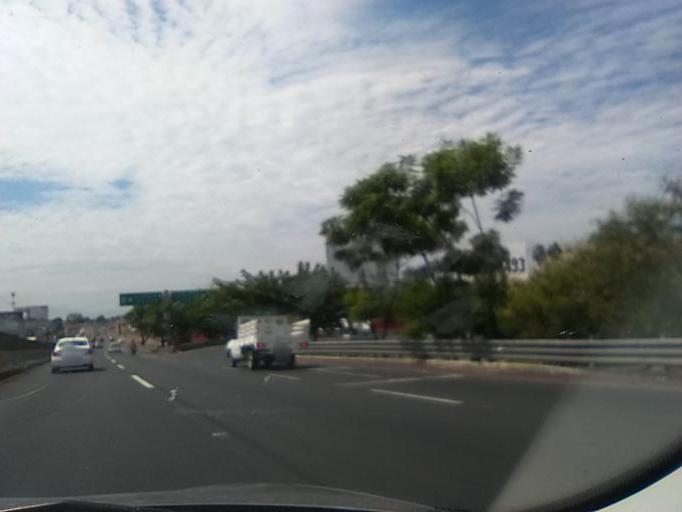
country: MX
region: Morelos
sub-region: Cuernavaca
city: Cuernavaca
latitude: 18.9208
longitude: -99.2031
